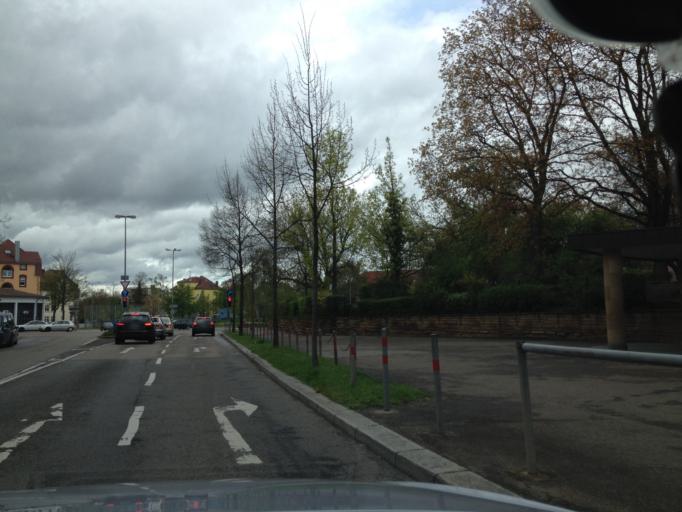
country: DE
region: Baden-Wuerttemberg
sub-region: Regierungsbezirk Stuttgart
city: Heilbronn
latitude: 49.1330
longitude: 9.2290
